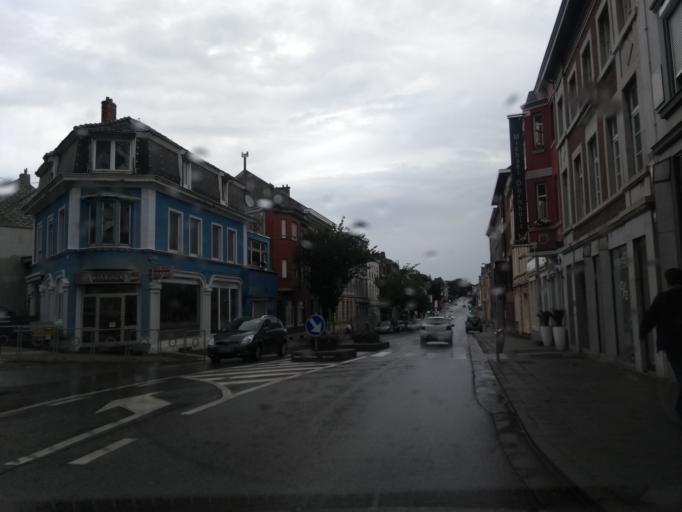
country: BE
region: Wallonia
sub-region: Province de Liege
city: Eupen
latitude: 50.6322
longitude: 6.0305
